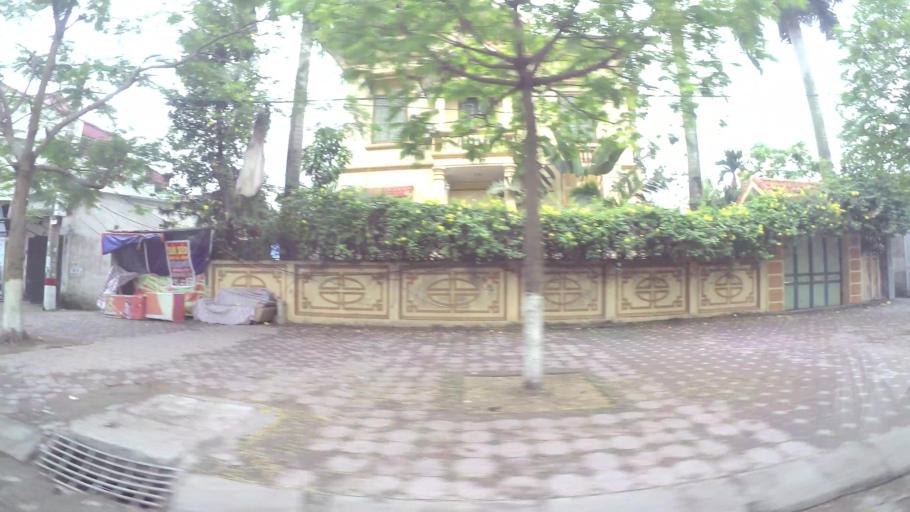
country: VN
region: Ha Noi
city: Van Dien
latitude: 20.9730
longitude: 105.8486
